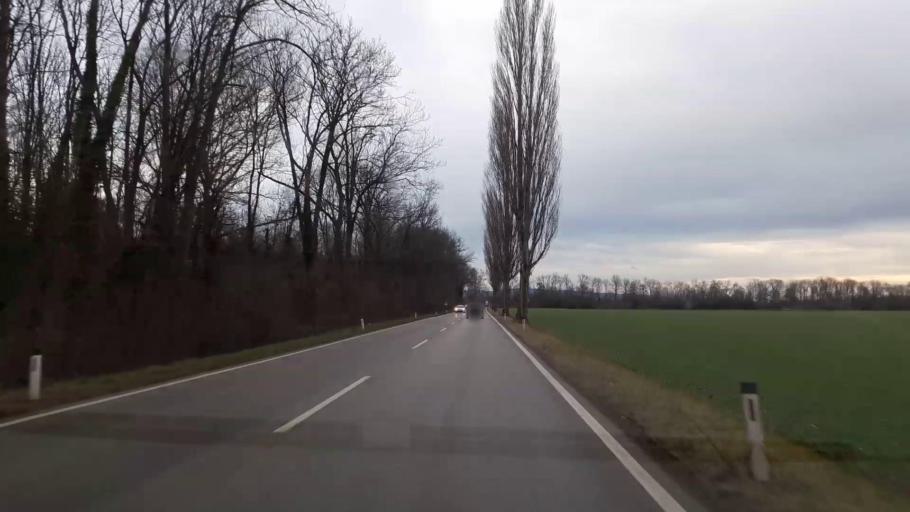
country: AT
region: Lower Austria
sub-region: Politischer Bezirk Baden
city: Ebreichsdorf
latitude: 47.9615
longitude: 16.3900
